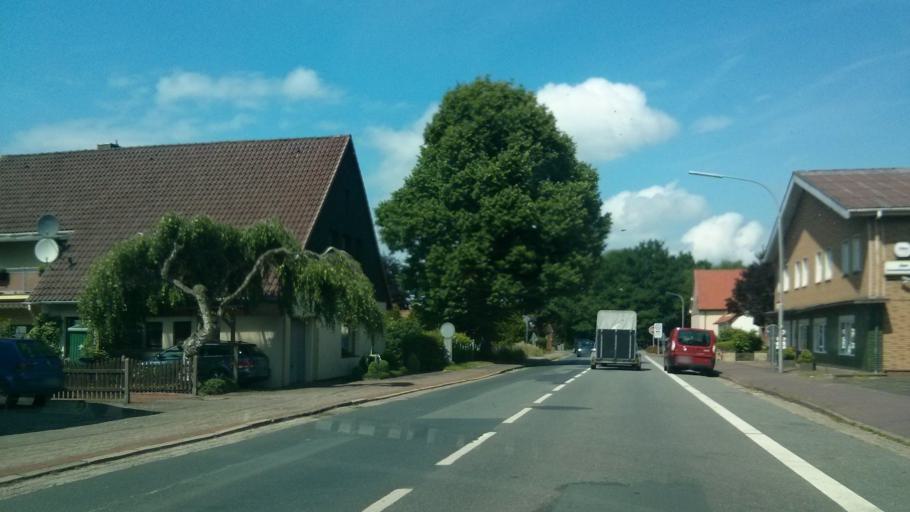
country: DE
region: Lower Saxony
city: Elmlohe
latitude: 53.5163
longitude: 8.7240
